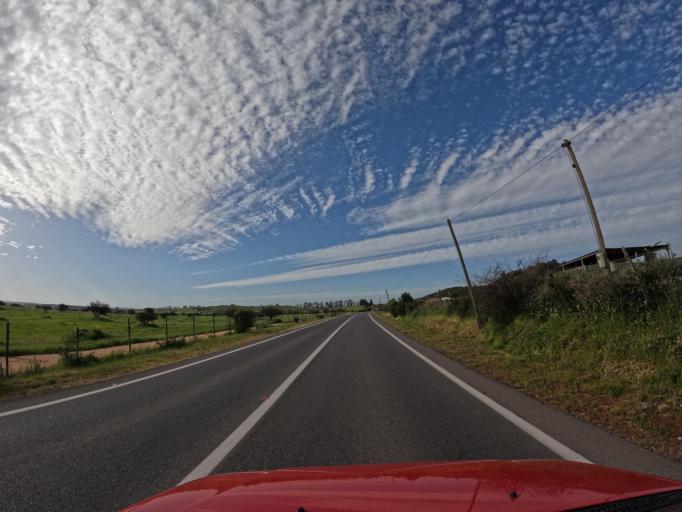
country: CL
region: O'Higgins
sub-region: Provincia de Colchagua
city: Santa Cruz
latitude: -34.2012
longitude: -71.7360
